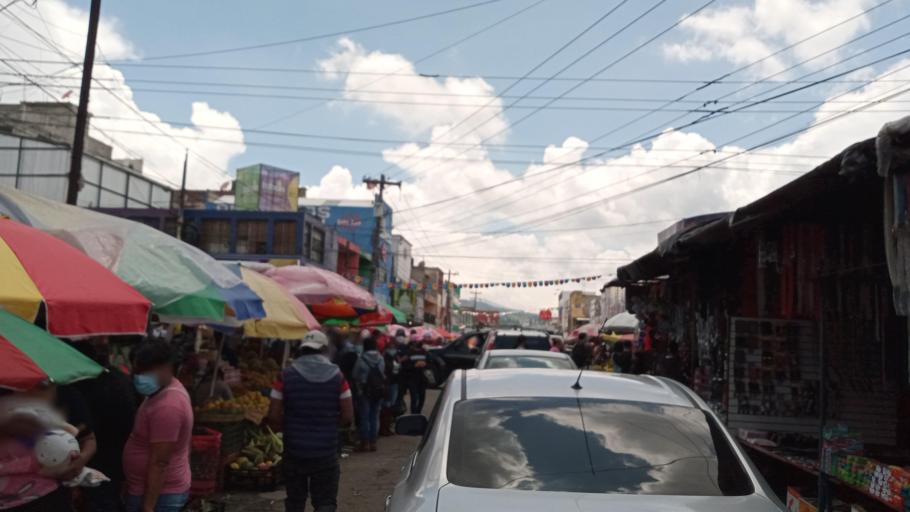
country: GT
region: Quetzaltenango
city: Quetzaltenango
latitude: 14.8415
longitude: -91.5204
